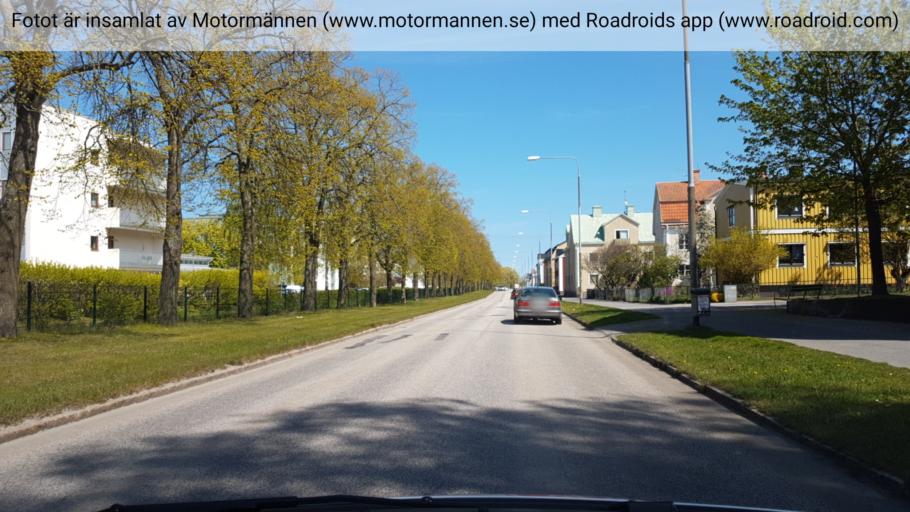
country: SE
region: Kalmar
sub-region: Vasterviks Kommun
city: Vaestervik
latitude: 57.7534
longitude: 16.6323
